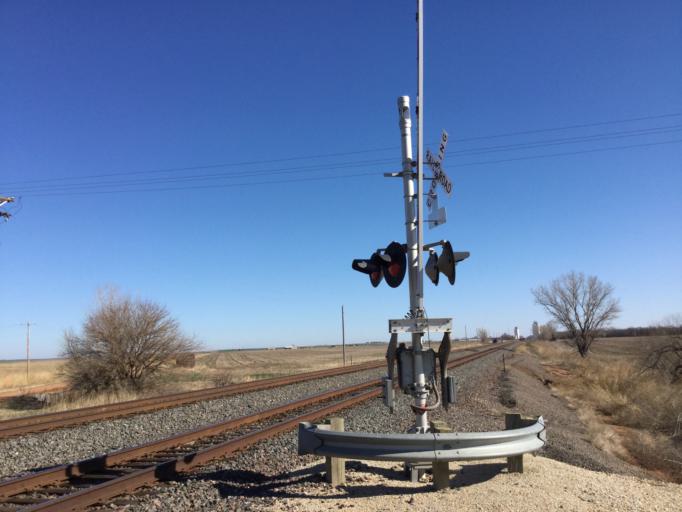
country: US
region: Kansas
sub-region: Barber County
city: Kiowa
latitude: 36.9987
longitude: -98.5035
